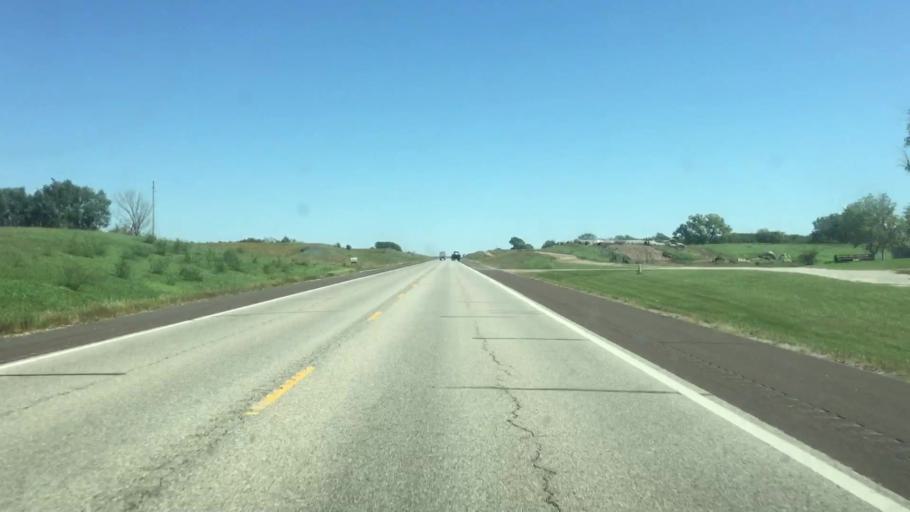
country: US
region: Kansas
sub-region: Nemaha County
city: Seneca
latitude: 39.8421
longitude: -96.2878
